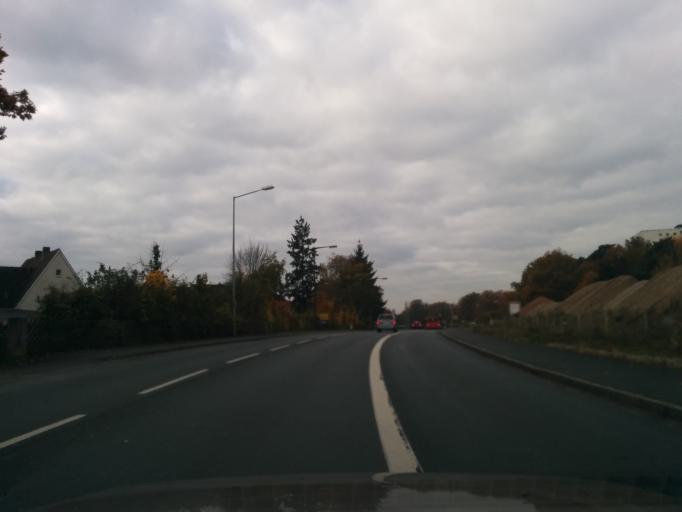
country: DE
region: Bavaria
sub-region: Regierungsbezirk Mittelfranken
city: Buckenhof
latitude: 49.5967
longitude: 11.0568
